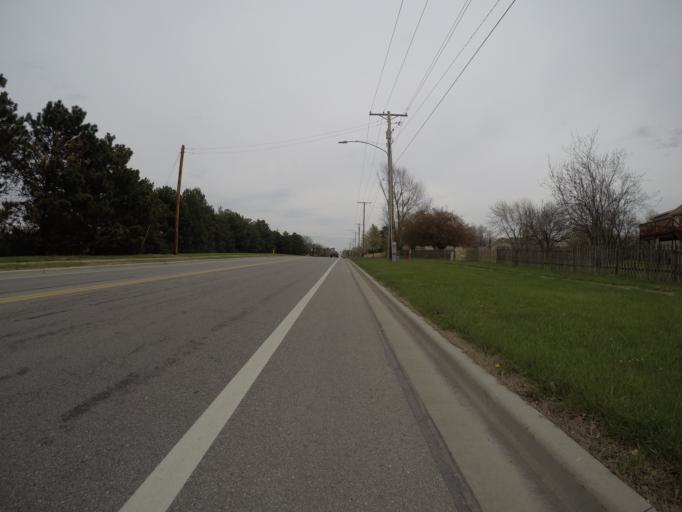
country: US
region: Kansas
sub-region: Johnson County
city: Olathe
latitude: 38.8691
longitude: -94.7818
